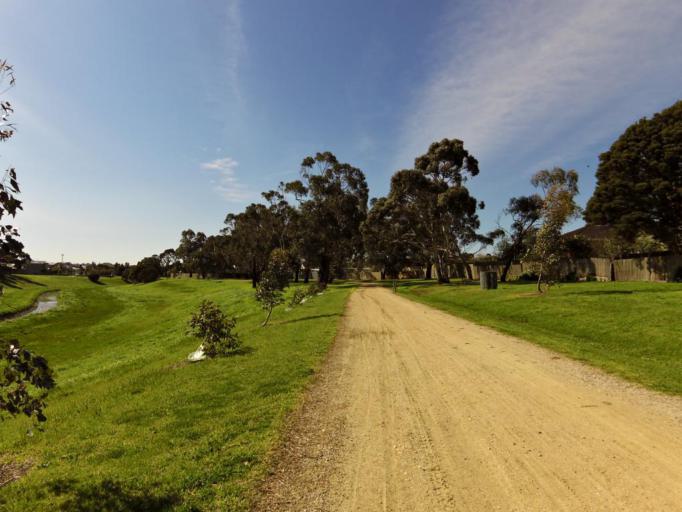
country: AU
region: Victoria
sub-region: Greater Dandenong
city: Dandenong
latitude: -37.9958
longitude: 145.2004
